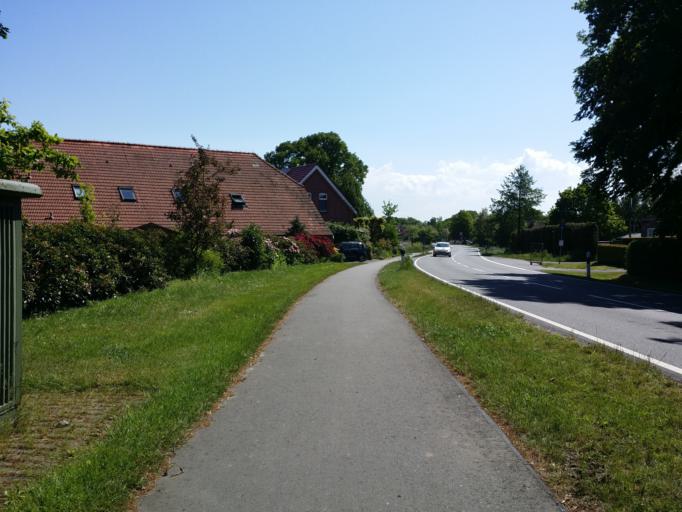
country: DE
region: Lower Saxony
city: Esens
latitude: 53.6556
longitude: 7.6136
